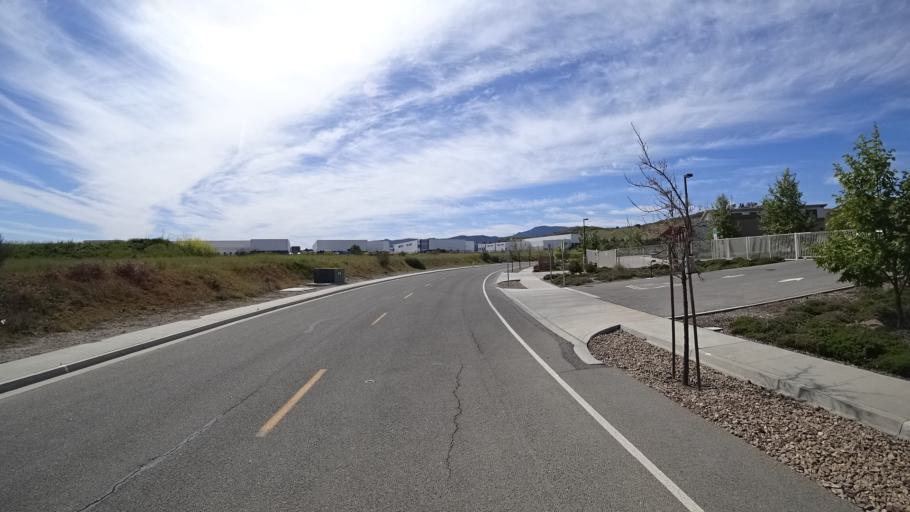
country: US
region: California
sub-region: Ventura County
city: Casa Conejo
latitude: 34.2045
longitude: -118.9331
